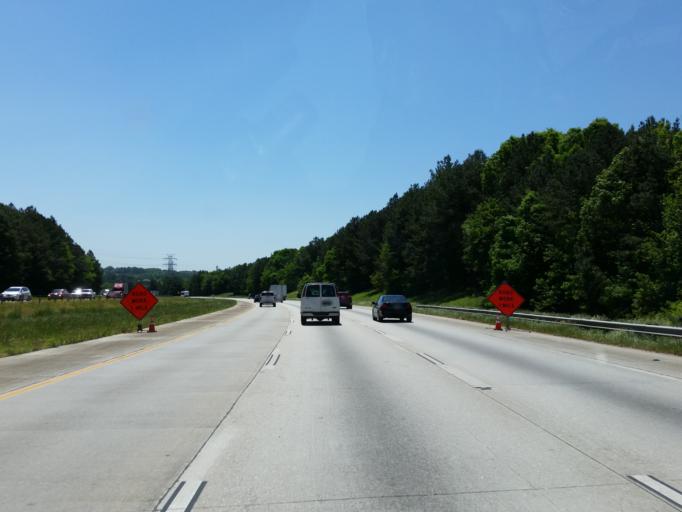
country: US
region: Georgia
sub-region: Clayton County
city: Conley
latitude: 33.6551
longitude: -84.3249
